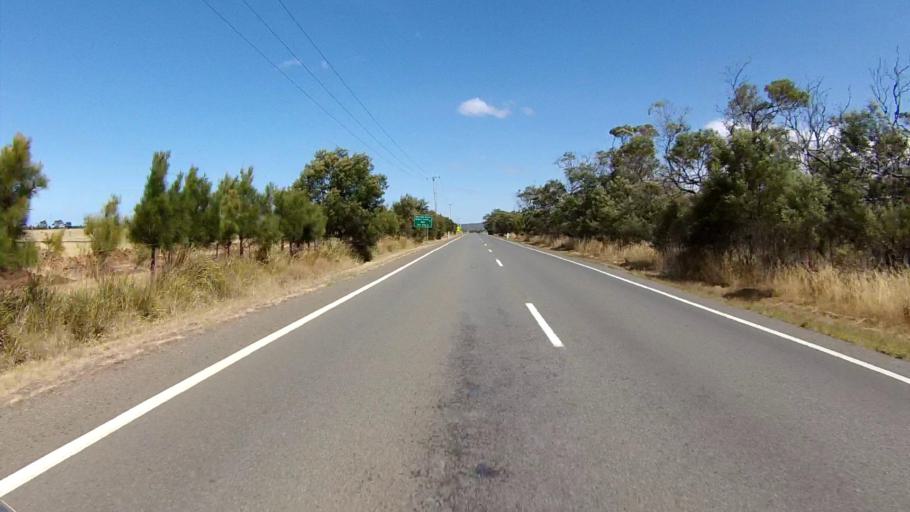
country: AU
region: Tasmania
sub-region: Break O'Day
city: St Helens
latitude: -42.0949
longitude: 148.0644
